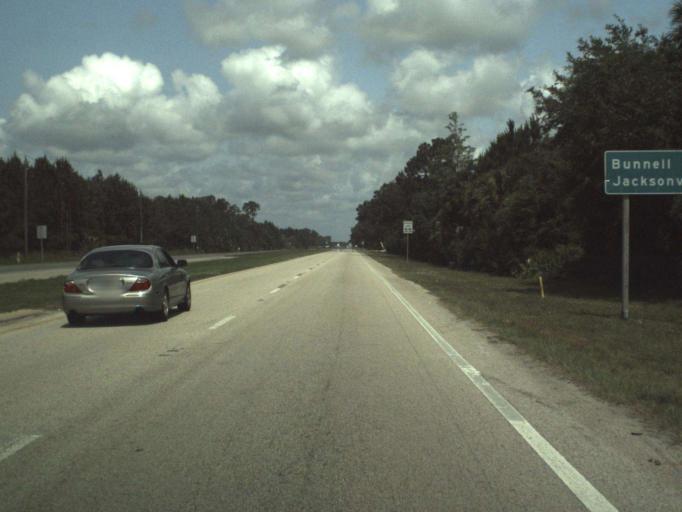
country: US
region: Florida
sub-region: Volusia County
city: Ormond-by-the-Sea
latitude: 29.3396
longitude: -81.1359
